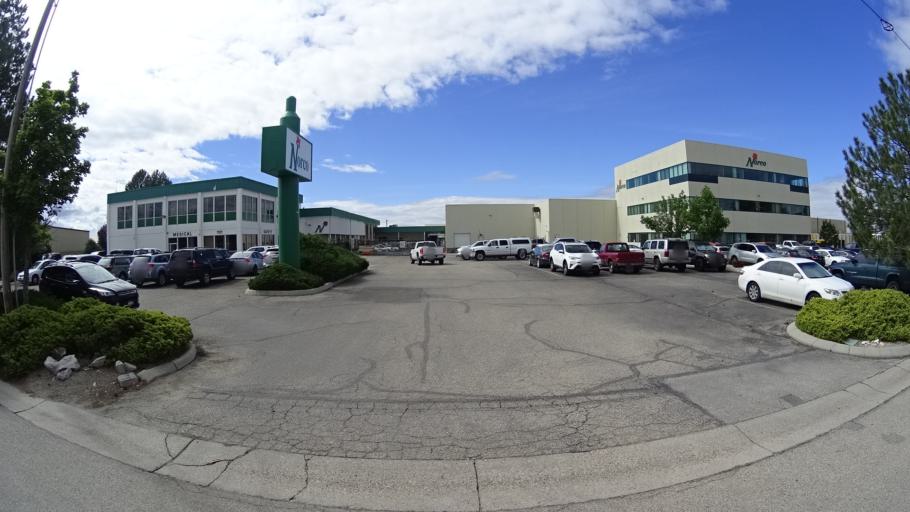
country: US
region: Idaho
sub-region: Ada County
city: Boise
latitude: 43.5604
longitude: -116.1955
